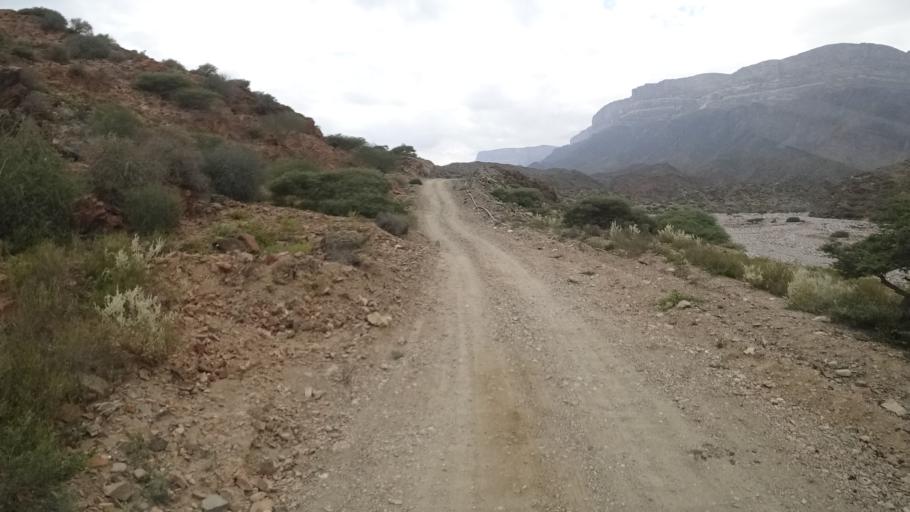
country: OM
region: Zufar
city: Salalah
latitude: 17.1715
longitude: 54.9575
